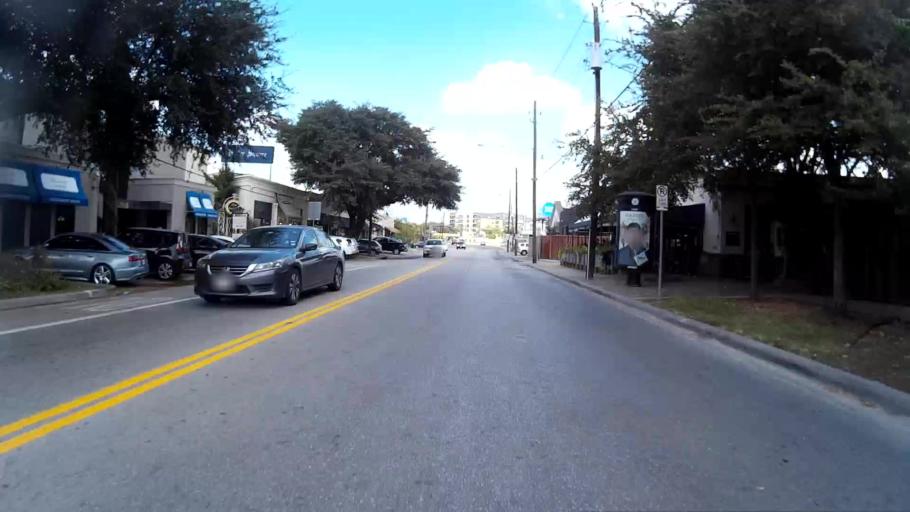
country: US
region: Texas
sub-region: Dallas County
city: Highland Park
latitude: 32.8203
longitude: -96.7847
